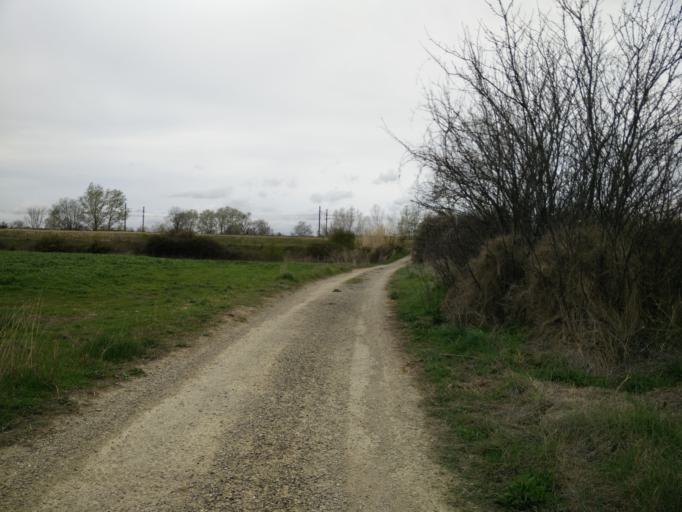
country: FR
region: Languedoc-Roussillon
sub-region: Departement du Gard
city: Gallargues-le-Montueux
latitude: 43.7114
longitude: 4.1672
